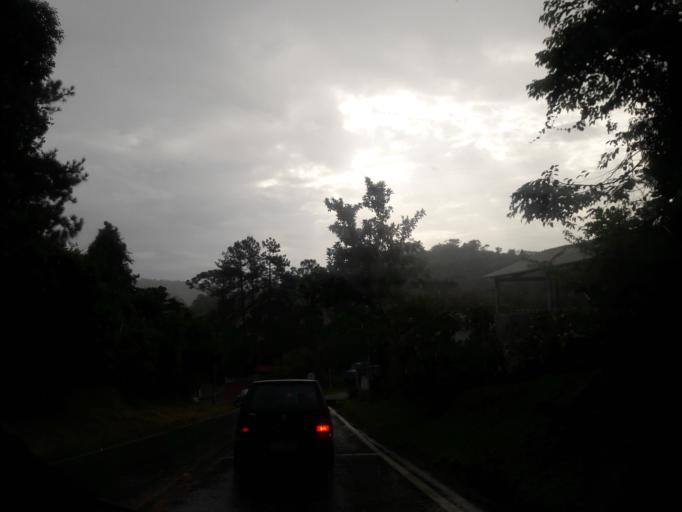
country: BR
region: Sao Paulo
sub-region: Aruja
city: Aruja
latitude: -23.3052
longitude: -46.4362
